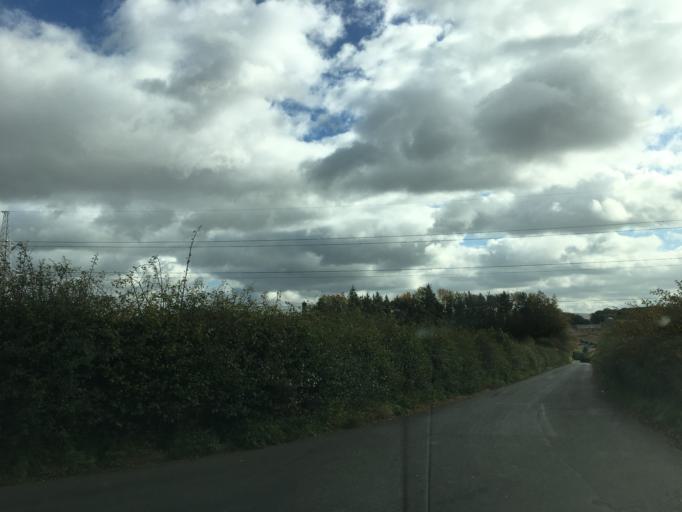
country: GB
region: Scotland
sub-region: East Lothian
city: Pencaitland
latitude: 55.8932
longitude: -2.8942
